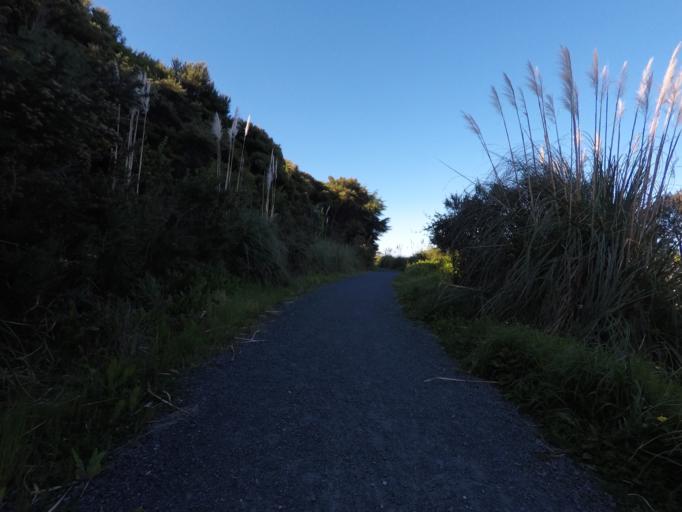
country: NZ
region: Auckland
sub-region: Auckland
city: Rosebank
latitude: -36.8450
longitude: 174.6560
